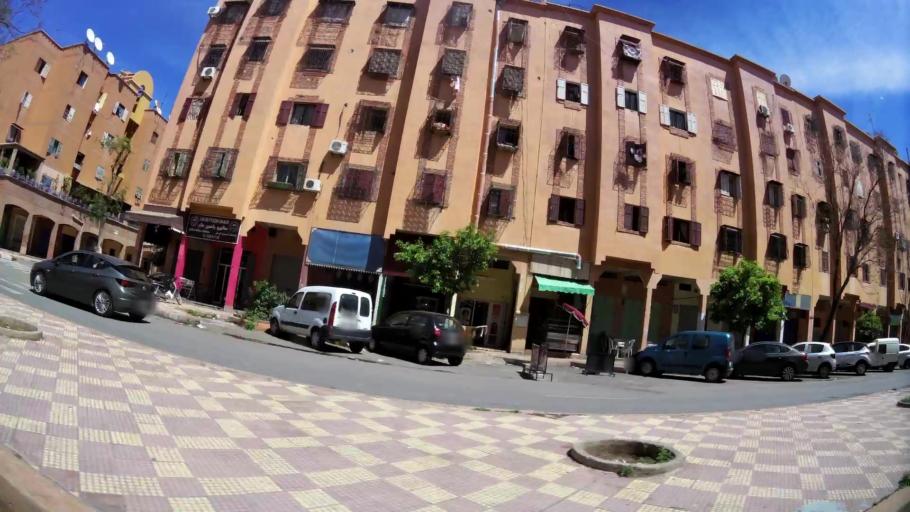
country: MA
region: Marrakech-Tensift-Al Haouz
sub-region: Marrakech
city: Marrakesh
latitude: 31.6432
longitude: -8.0654
